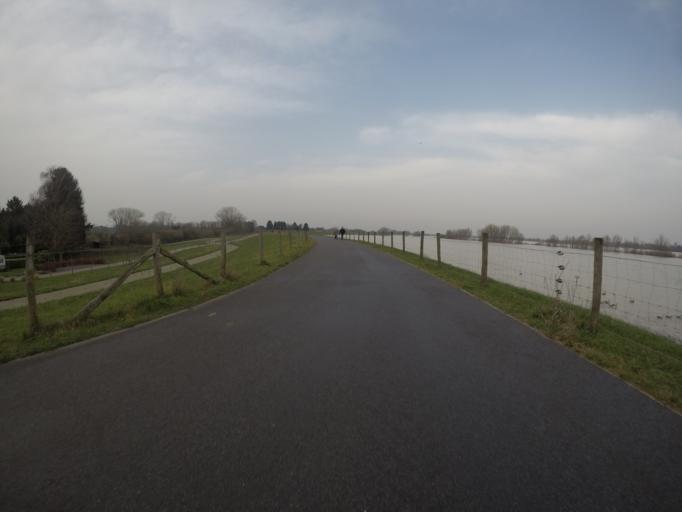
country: DE
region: North Rhine-Westphalia
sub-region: Regierungsbezirk Dusseldorf
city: Xanten
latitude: 51.7072
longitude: 6.4207
